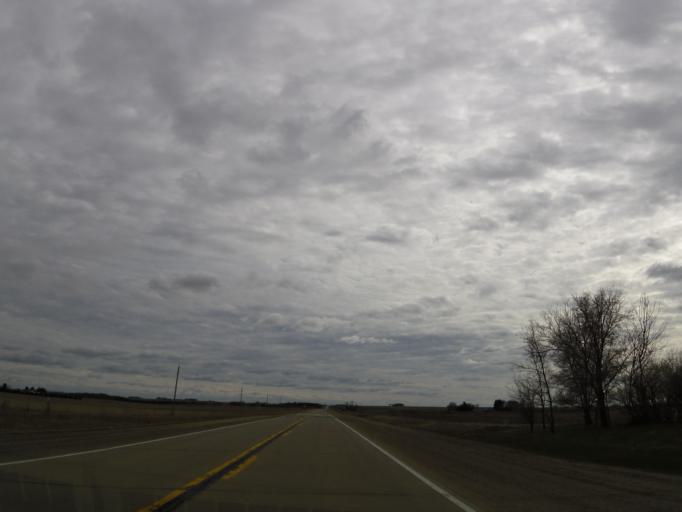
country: US
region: Iowa
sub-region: Howard County
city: Cresco
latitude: 43.4056
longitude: -92.2987
